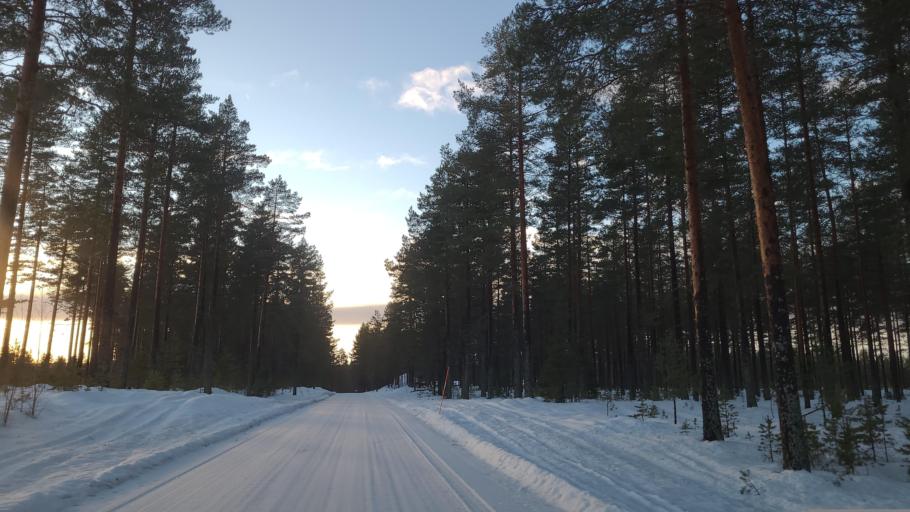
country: SE
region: Gaevleborg
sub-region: Bollnas Kommun
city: Kilafors
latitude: 61.3671
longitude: 16.6663
